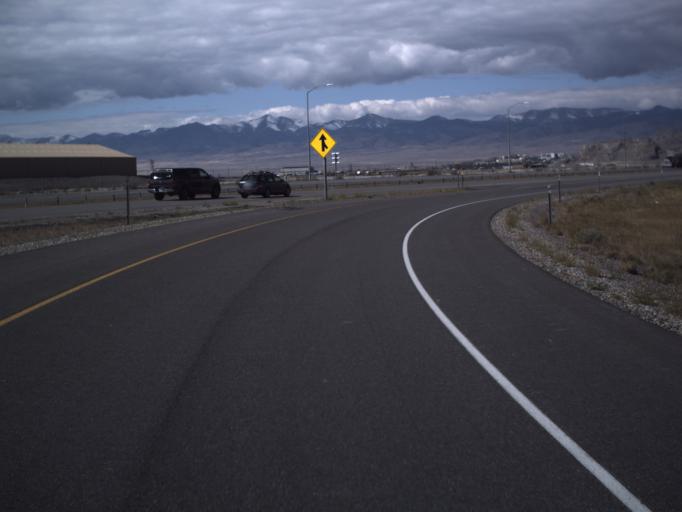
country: US
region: Utah
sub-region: Tooele County
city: Wendover
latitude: 40.7429
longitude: -113.9735
